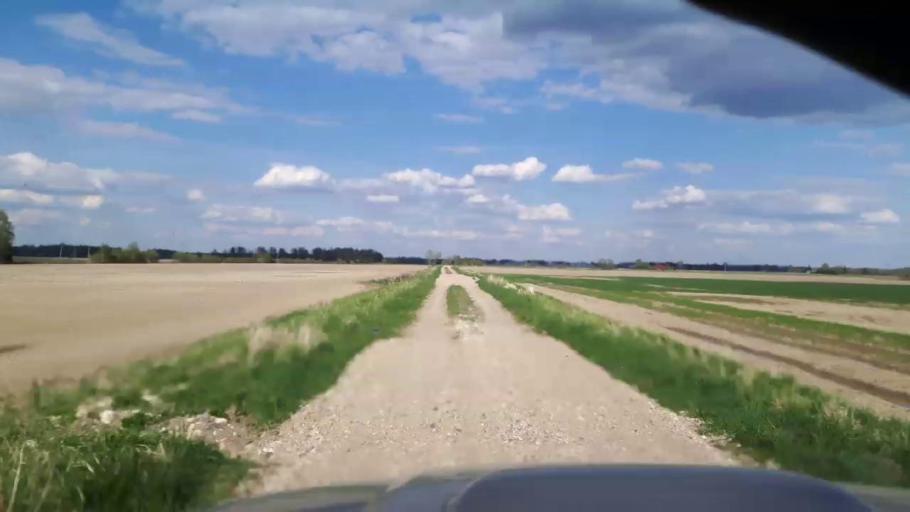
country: EE
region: Paernumaa
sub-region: Sindi linn
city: Sindi
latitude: 58.4342
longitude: 24.7448
